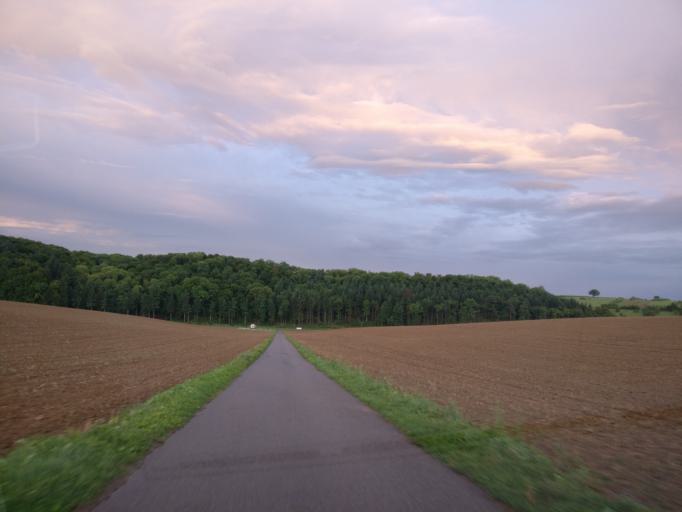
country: DE
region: Baden-Wuerttemberg
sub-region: Karlsruhe Region
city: Konigsbach-Stein
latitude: 48.9813
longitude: 8.5996
